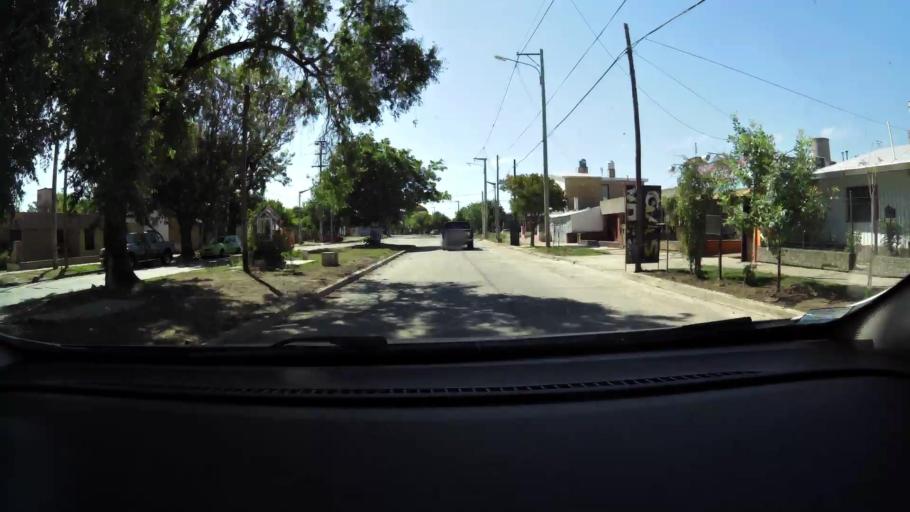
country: AR
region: Cordoba
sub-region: Departamento de Capital
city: Cordoba
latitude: -31.3681
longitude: -64.1684
